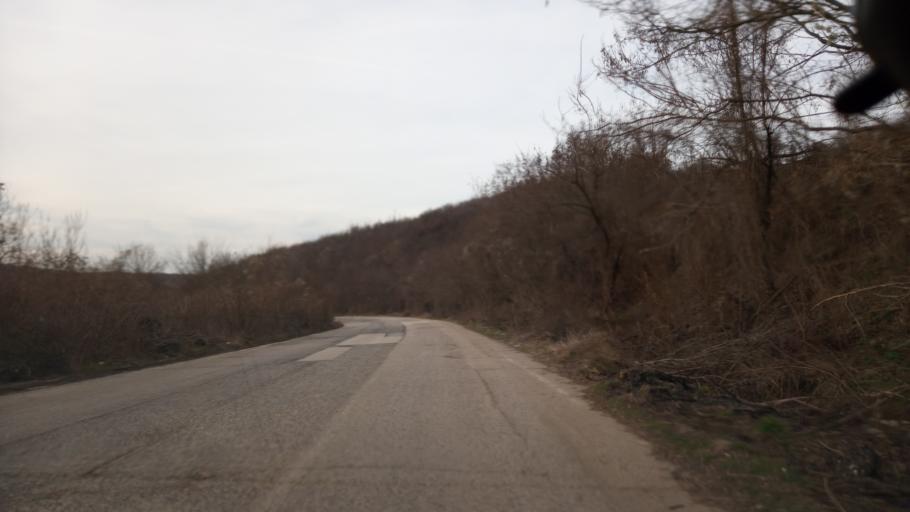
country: BG
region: Pleven
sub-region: Obshtina Nikopol
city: Nikopol
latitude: 43.5939
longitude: 24.9528
